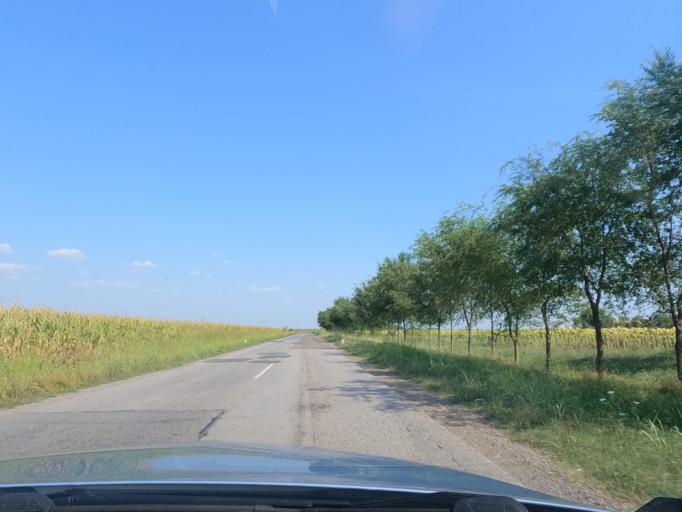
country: RS
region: Autonomna Pokrajina Vojvodina
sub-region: Juznobacki Okrug
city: Becej
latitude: 45.6517
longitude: 19.9722
